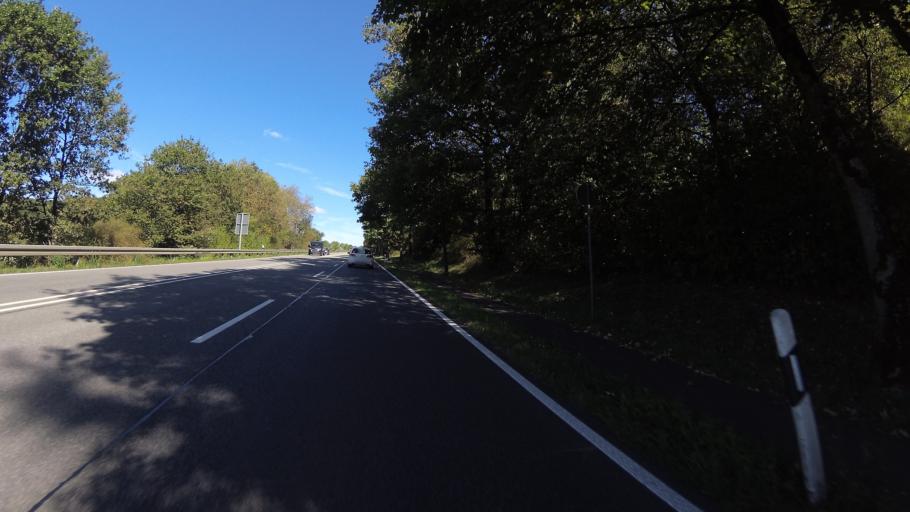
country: DE
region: Saarland
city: Tholey
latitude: 49.4694
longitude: 7.0081
